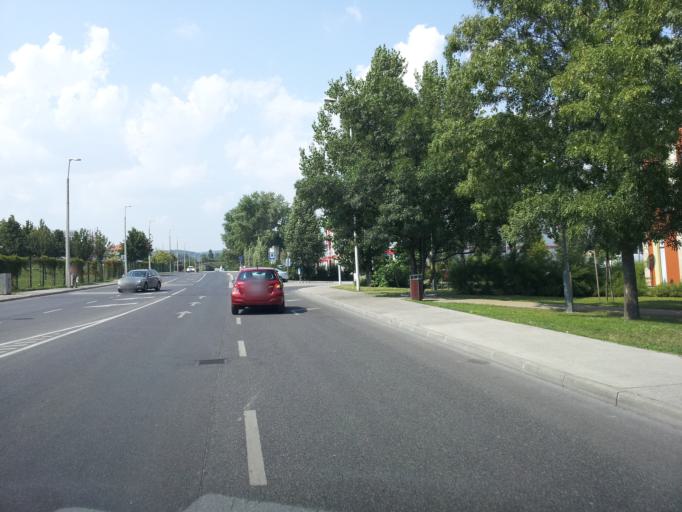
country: HU
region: Veszprem
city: Balatonfured
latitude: 46.9474
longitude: 17.8757
